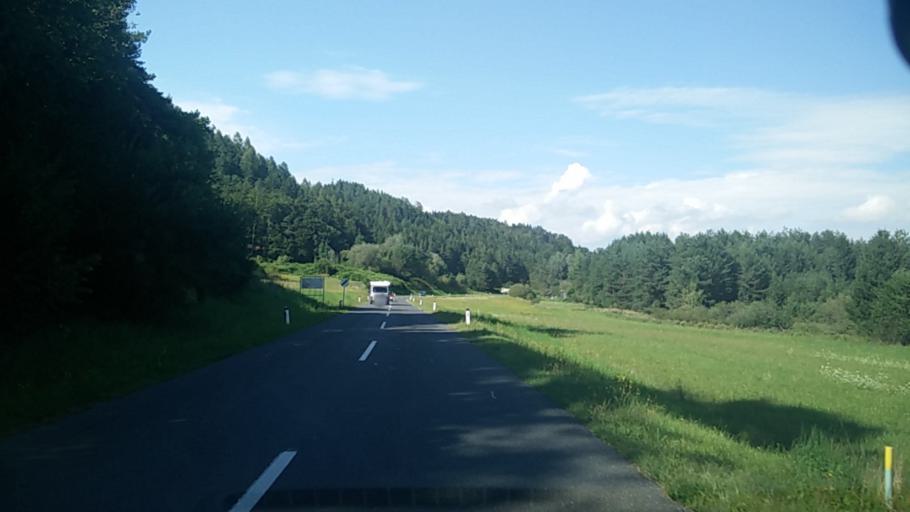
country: AT
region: Carinthia
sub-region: Politischer Bezirk Volkermarkt
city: Sittersdorf
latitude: 46.5932
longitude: 14.5667
